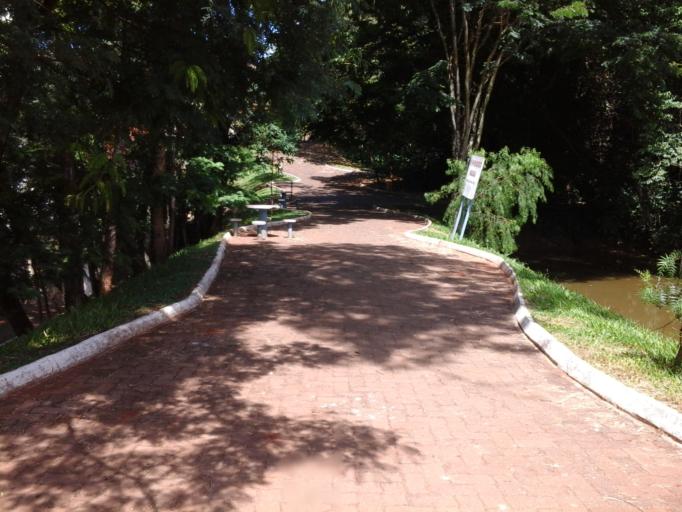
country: BR
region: Minas Gerais
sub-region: Patos De Minas
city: Patos de Minas
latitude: -18.5838
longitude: -46.5049
